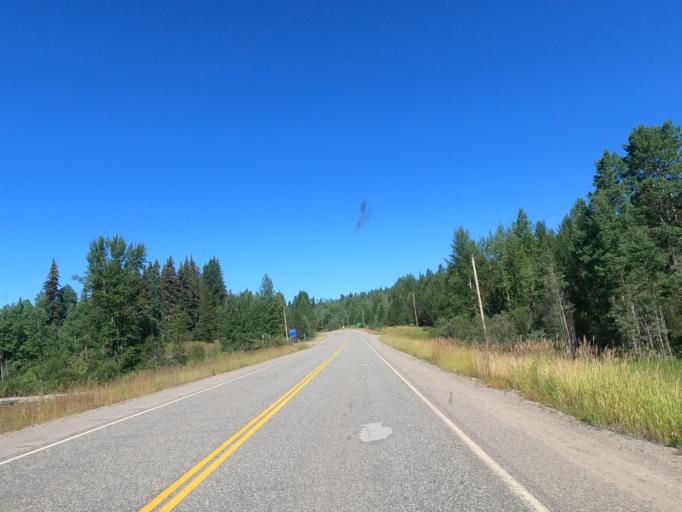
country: CA
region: British Columbia
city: Quesnel
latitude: 53.0502
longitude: -122.1528
